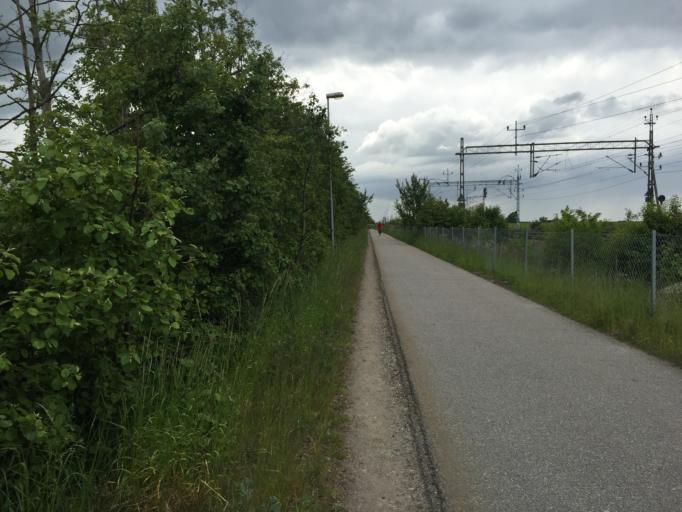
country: SE
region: Skane
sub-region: Lunds Kommun
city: Lund
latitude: 55.7428
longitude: 13.1940
